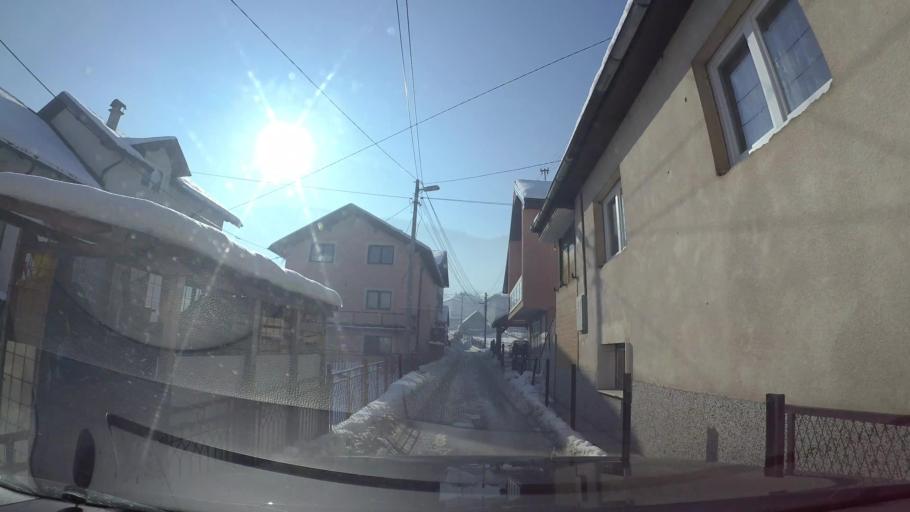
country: BA
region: Federation of Bosnia and Herzegovina
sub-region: Kanton Sarajevo
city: Sarajevo
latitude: 43.7943
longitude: 18.3171
